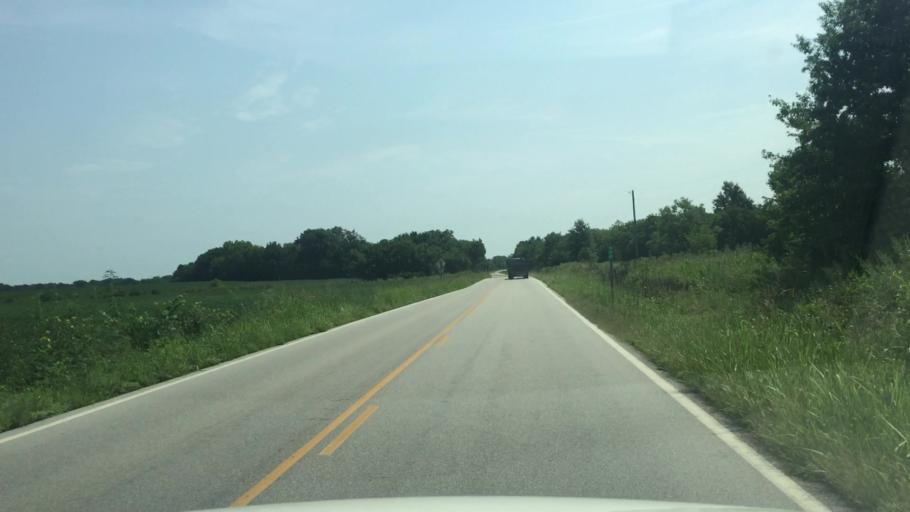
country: US
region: Kansas
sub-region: Montgomery County
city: Cherryvale
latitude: 37.1938
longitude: -95.5555
